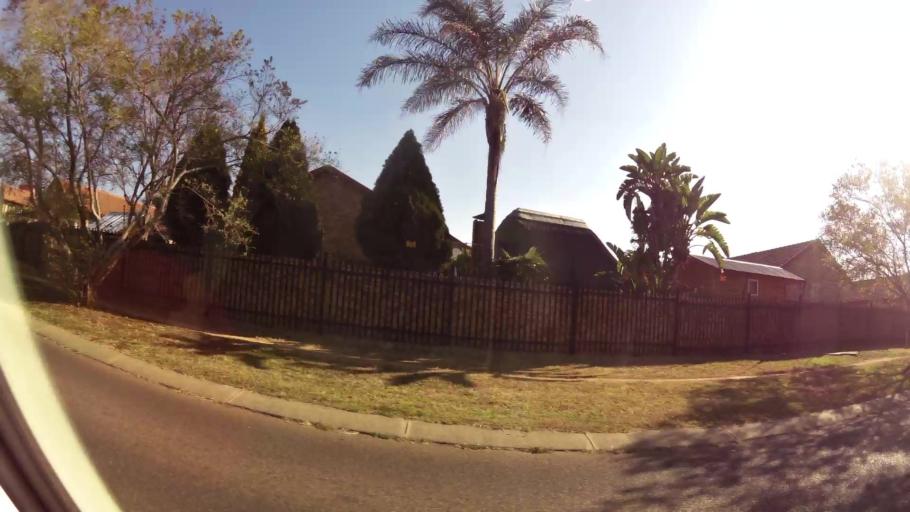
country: ZA
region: Gauteng
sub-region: City of Tshwane Metropolitan Municipality
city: Pretoria
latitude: -25.8018
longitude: 28.3025
